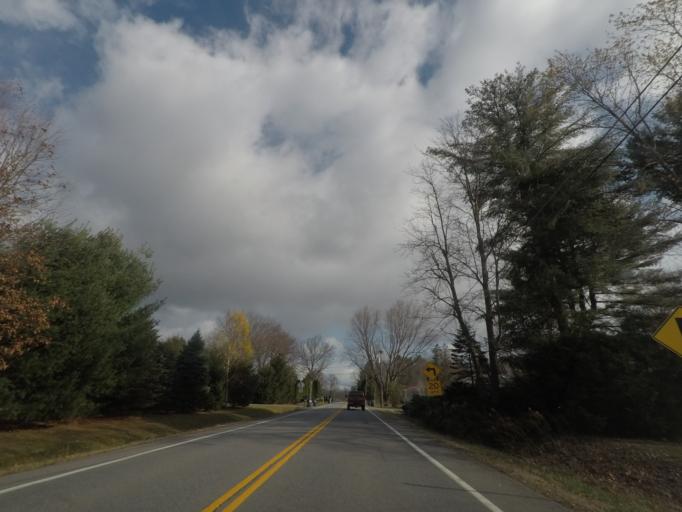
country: US
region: New York
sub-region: Saratoga County
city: Country Knolls
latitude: 42.9270
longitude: -73.8406
